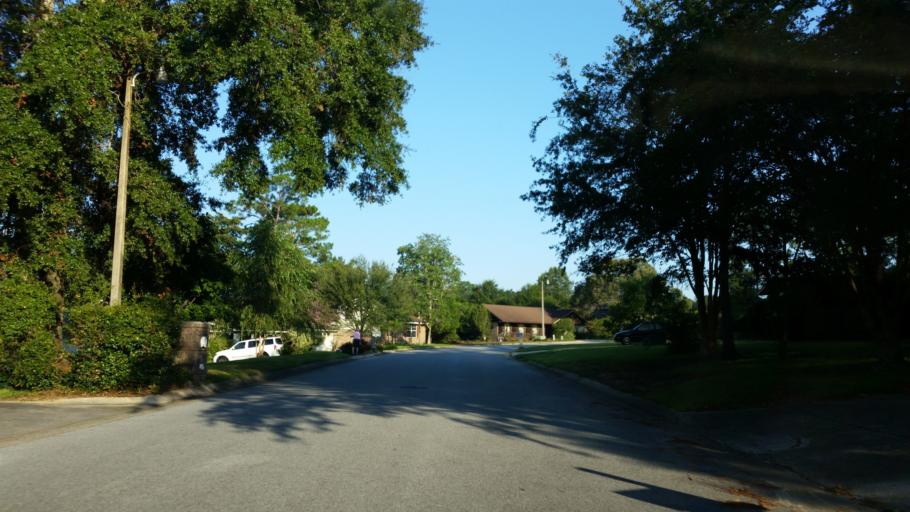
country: US
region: Florida
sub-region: Escambia County
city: Ensley
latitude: 30.5456
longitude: -87.2439
